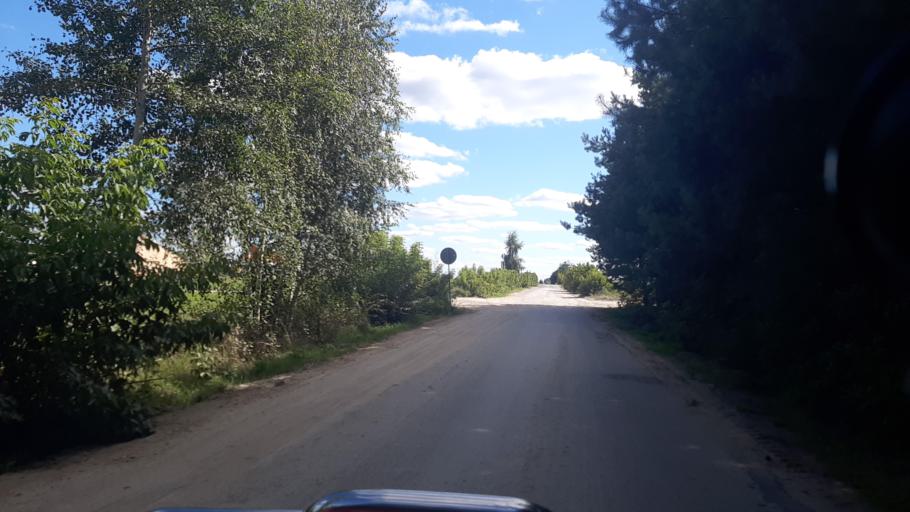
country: PL
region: Lublin Voivodeship
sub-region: Powiat pulawski
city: Markuszow
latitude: 51.4138
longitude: 22.2296
